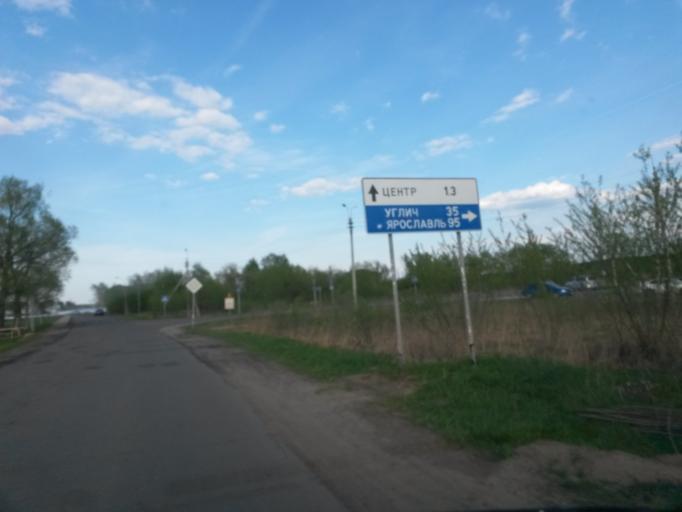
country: RU
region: Jaroslavl
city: Myshkin
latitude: 57.7815
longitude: 38.4504
